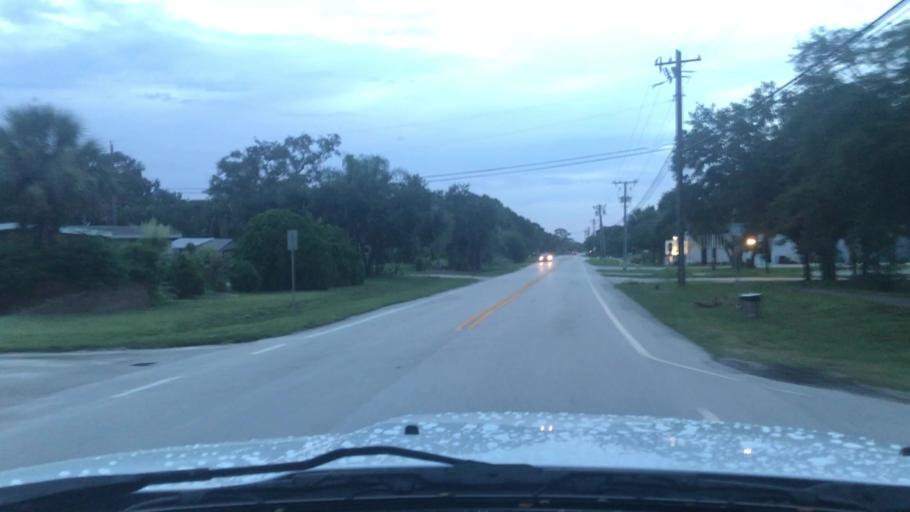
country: US
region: Florida
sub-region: Indian River County
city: Florida Ridge
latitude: 27.5948
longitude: -80.3833
